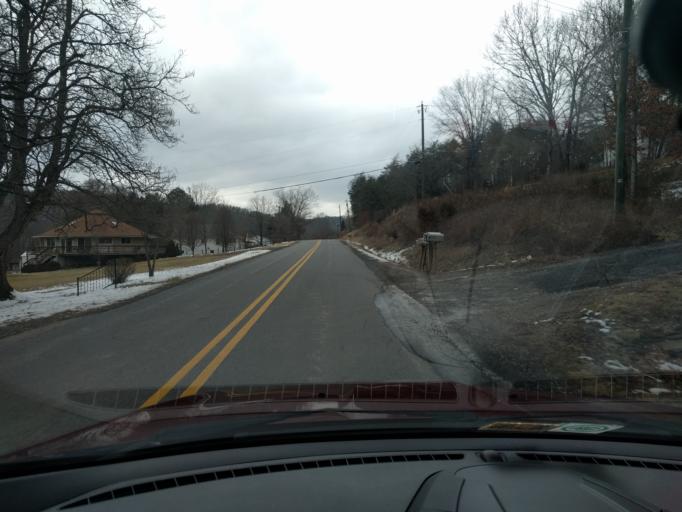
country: US
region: Virginia
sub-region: Alleghany County
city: Clifton Forge
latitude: 37.8416
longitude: -79.7484
